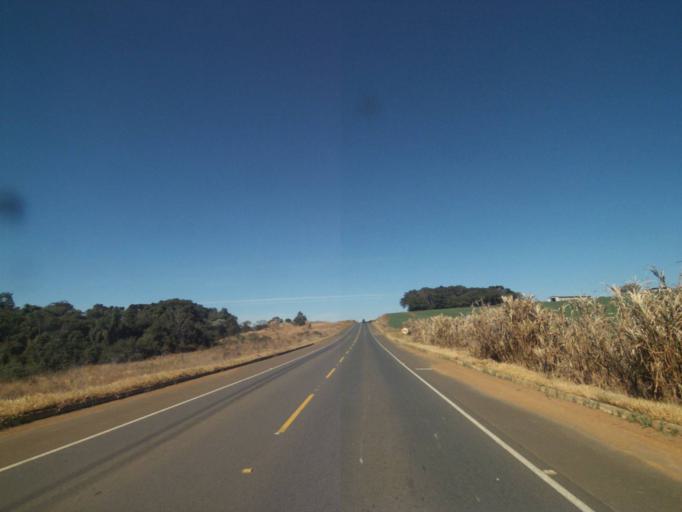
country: BR
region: Parana
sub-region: Tibagi
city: Tibagi
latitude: -24.5359
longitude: -50.4472
